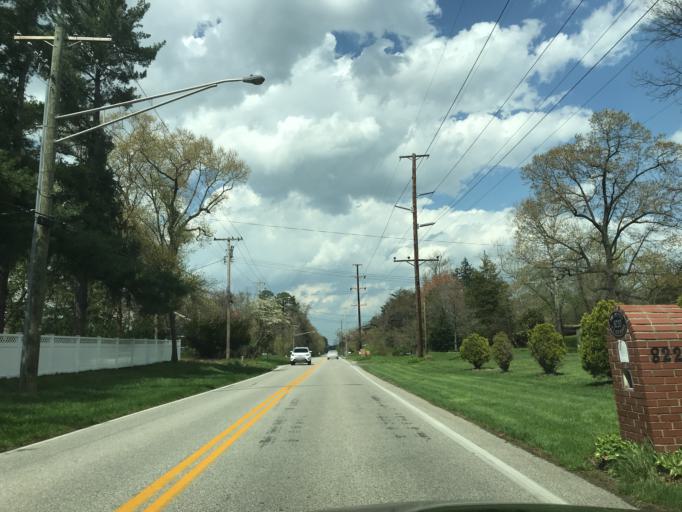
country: US
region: Maryland
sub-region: Anne Arundel County
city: Severn
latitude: 39.1207
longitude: -76.6797
